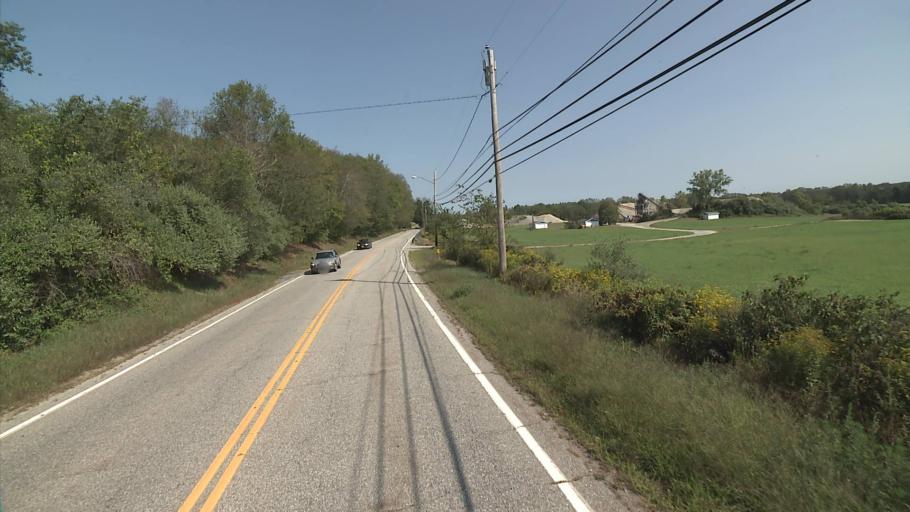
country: US
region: Connecticut
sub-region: Windham County
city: Plainfield Village
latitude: 41.6714
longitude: -71.9725
